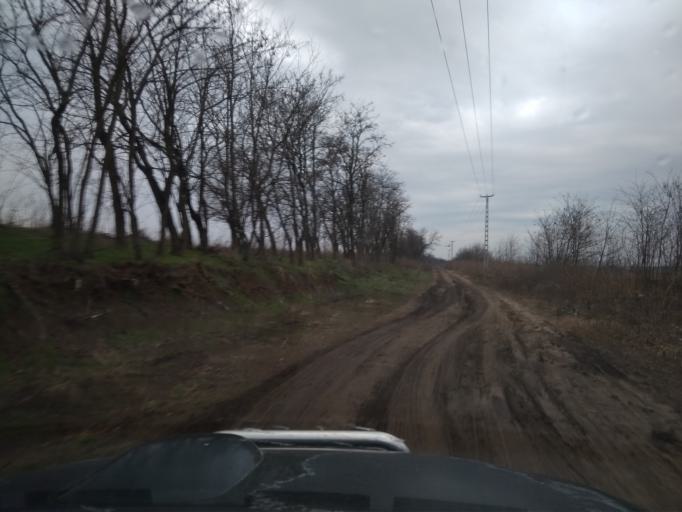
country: HU
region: Szabolcs-Szatmar-Bereg
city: Nyirpazony
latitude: 48.0004
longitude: 21.7891
